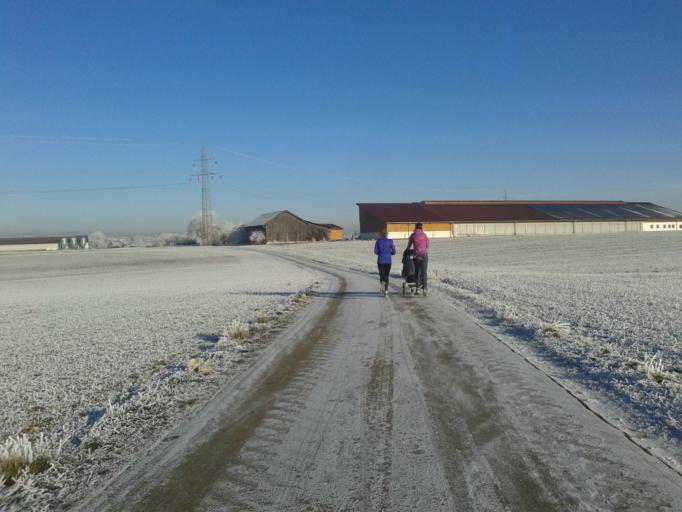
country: DE
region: Baden-Wuerttemberg
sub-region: Tuebingen Region
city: Dornstadt
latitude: 48.4375
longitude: 9.9629
